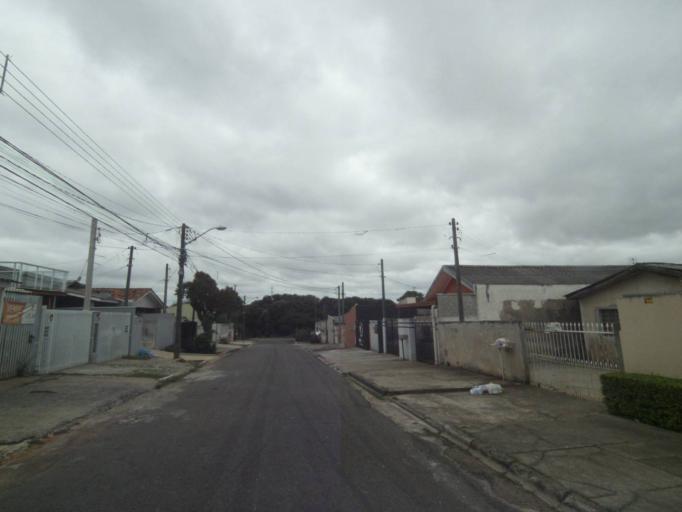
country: BR
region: Parana
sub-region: Sao Jose Dos Pinhais
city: Sao Jose dos Pinhais
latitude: -25.5438
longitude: -49.2710
